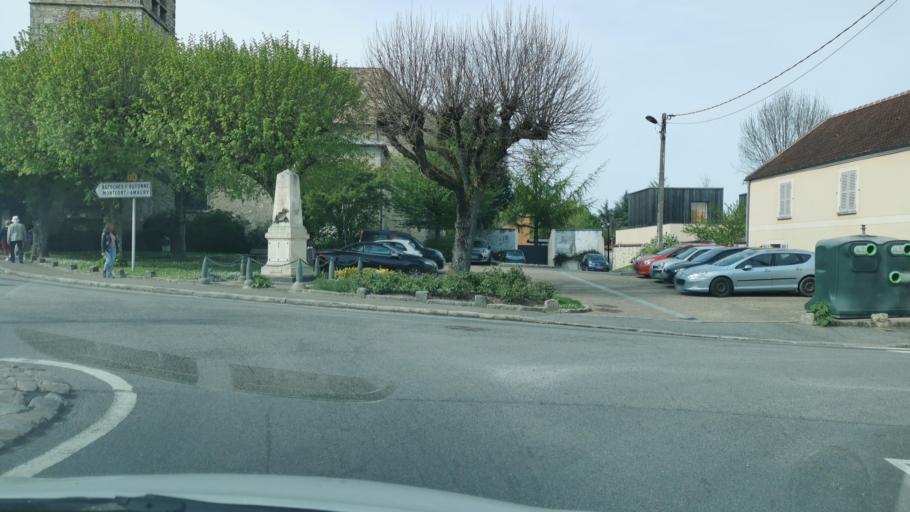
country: FR
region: Ile-de-France
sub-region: Departement des Yvelines
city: Jouars-Pontchartrain
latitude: 48.7778
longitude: 1.8772
